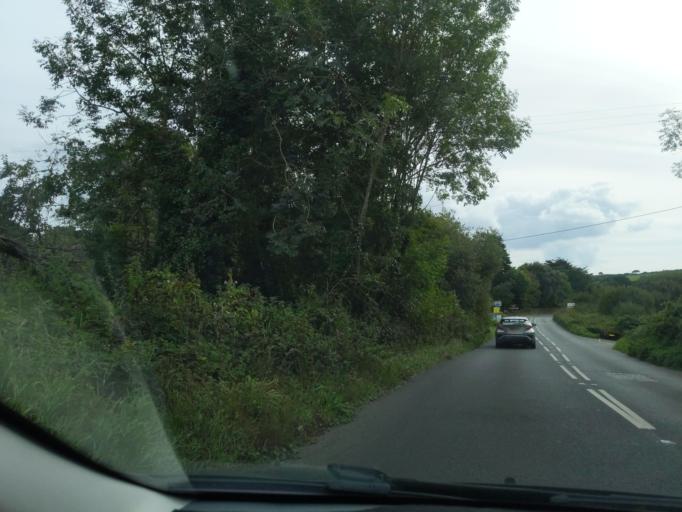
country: GB
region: England
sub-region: Cornwall
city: Mevagissey
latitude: 50.2929
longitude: -4.7864
